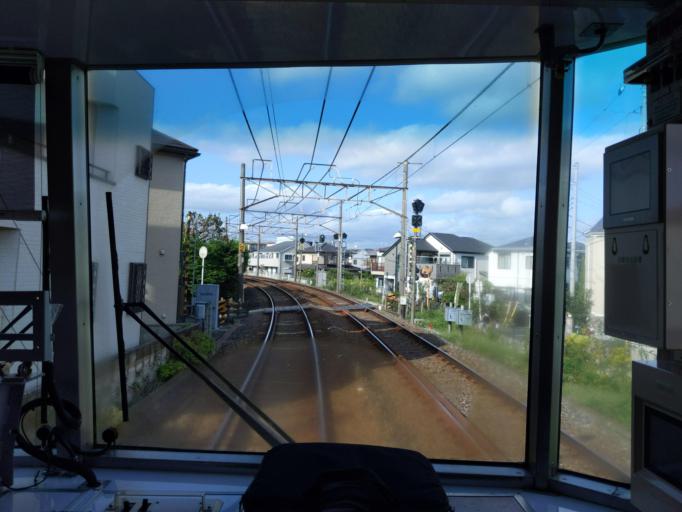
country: JP
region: Chiba
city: Kashiwa
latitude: 35.7880
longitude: 139.9772
